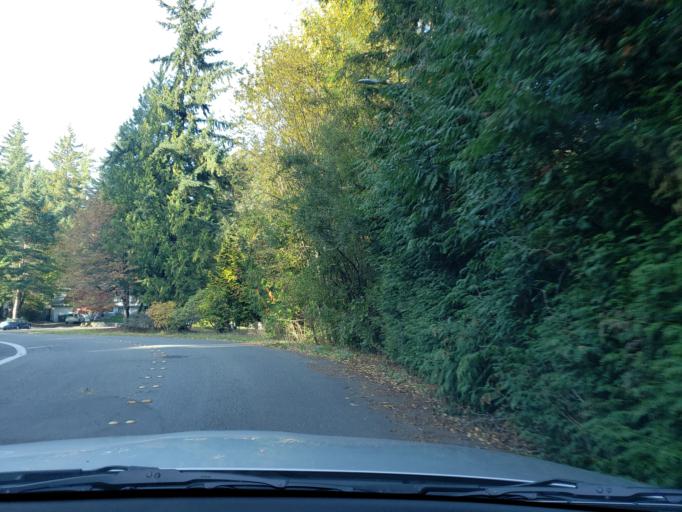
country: US
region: Washington
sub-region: Snohomish County
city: Meadowdale
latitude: 47.8685
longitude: -122.3174
